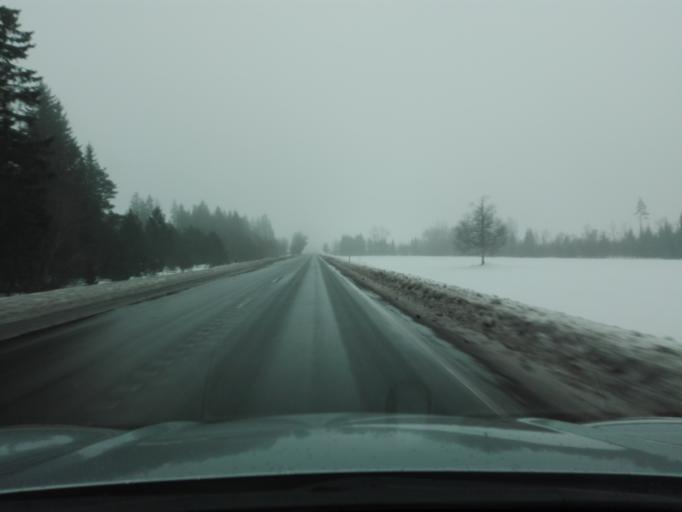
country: EE
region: Raplamaa
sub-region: Kohila vald
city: Kohila
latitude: 59.2055
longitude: 24.7809
